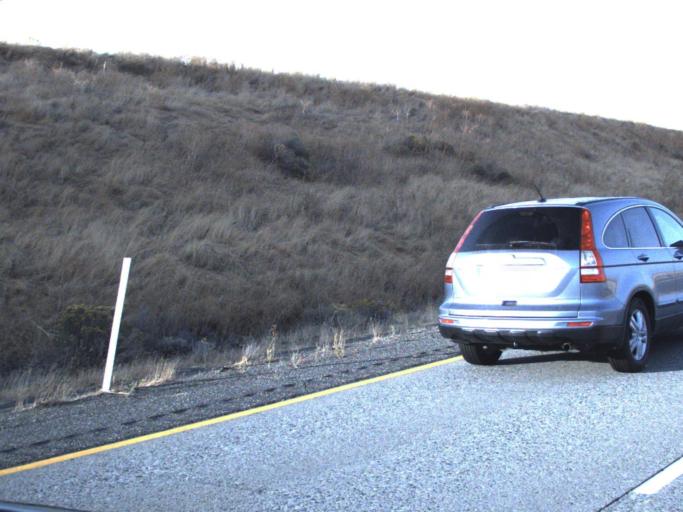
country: US
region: Washington
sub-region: Benton County
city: Highland
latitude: 46.1052
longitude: -119.2126
